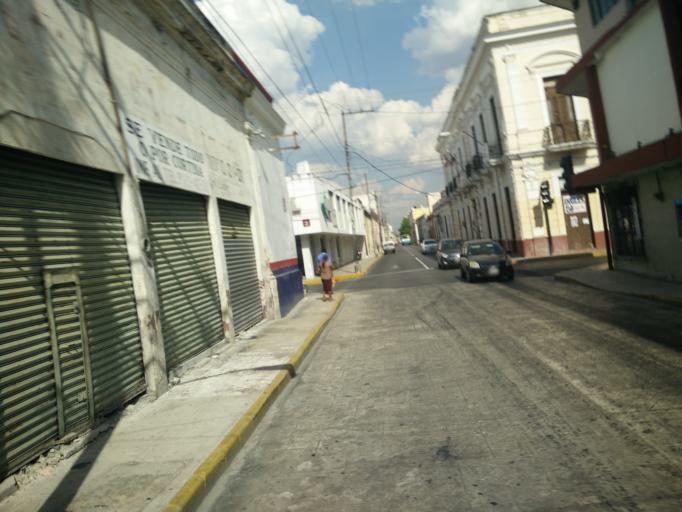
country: MX
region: Yucatan
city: Merida
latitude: 20.9693
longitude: -89.6188
